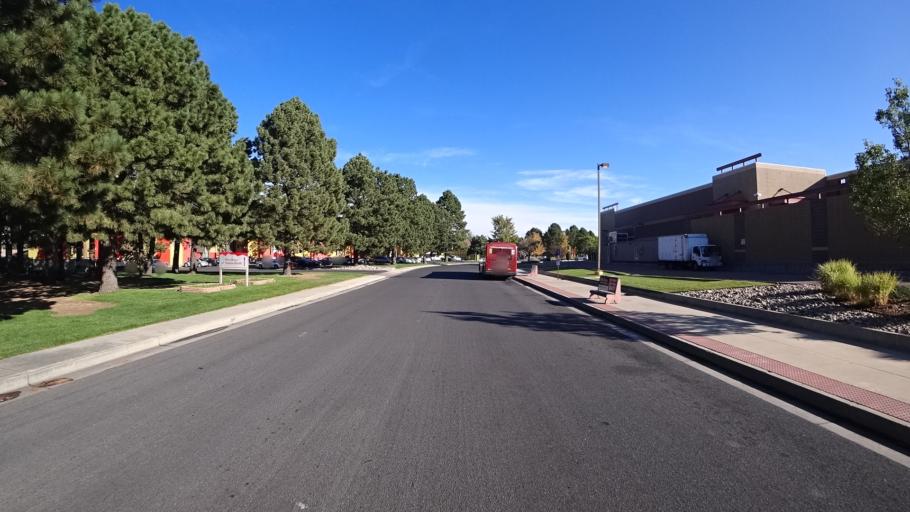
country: US
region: Colorado
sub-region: El Paso County
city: Cimarron Hills
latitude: 38.8919
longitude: -104.7617
